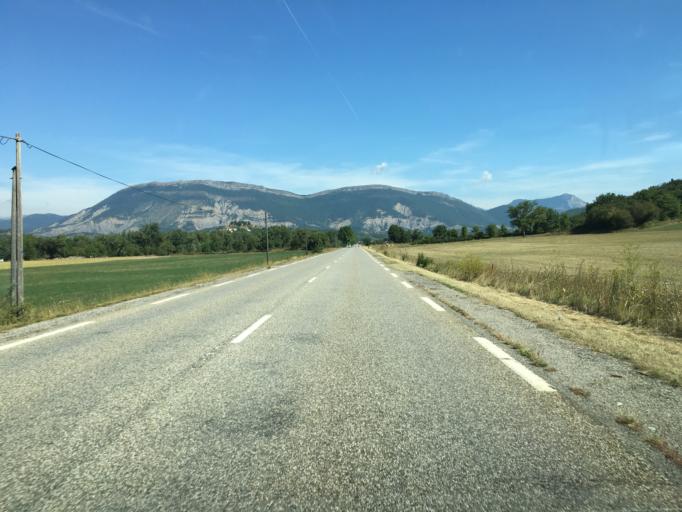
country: FR
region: Provence-Alpes-Cote d'Azur
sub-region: Departement des Hautes-Alpes
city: Serres
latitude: 44.4754
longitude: 5.7266
